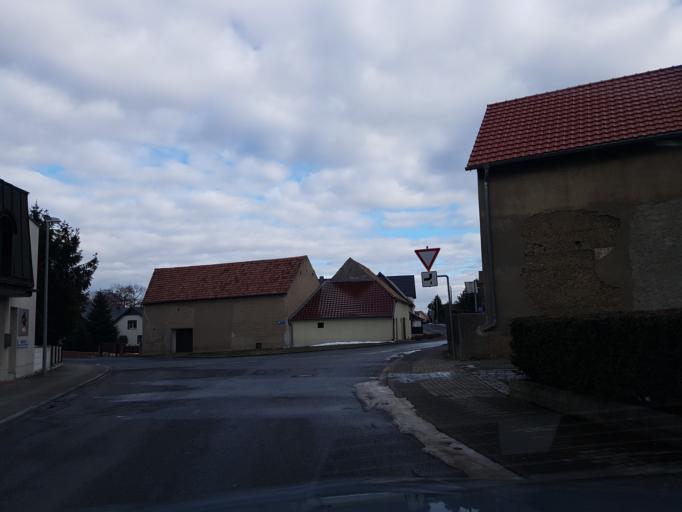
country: DE
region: Brandenburg
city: Merzdorf
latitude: 51.4019
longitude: 13.5339
